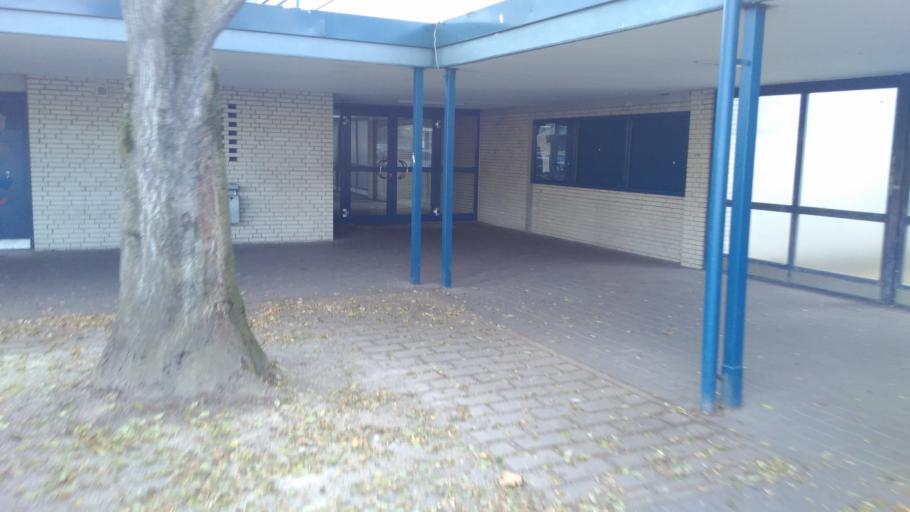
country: DE
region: North Rhine-Westphalia
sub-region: Regierungsbezirk Detmold
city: Verl
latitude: 51.8845
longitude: 8.5046
